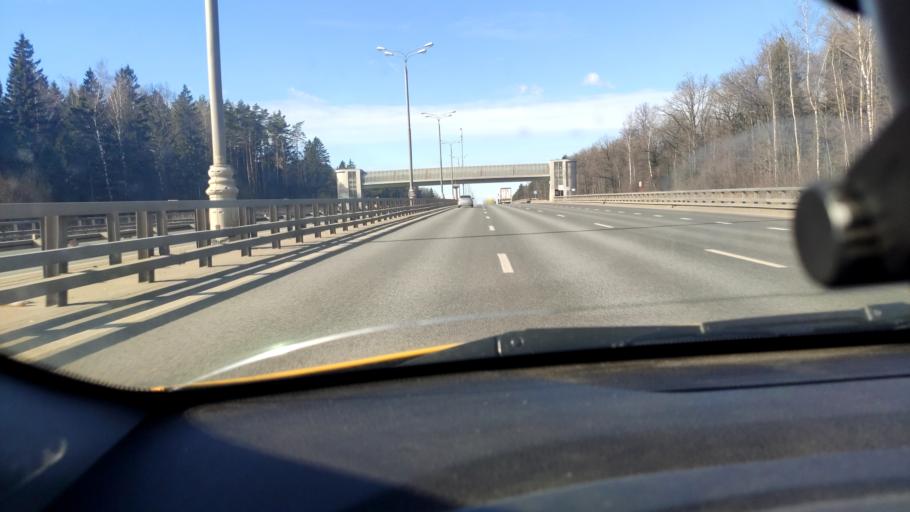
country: RU
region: Moskovskaya
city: Aprelevka
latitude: 55.5443
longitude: 37.1011
